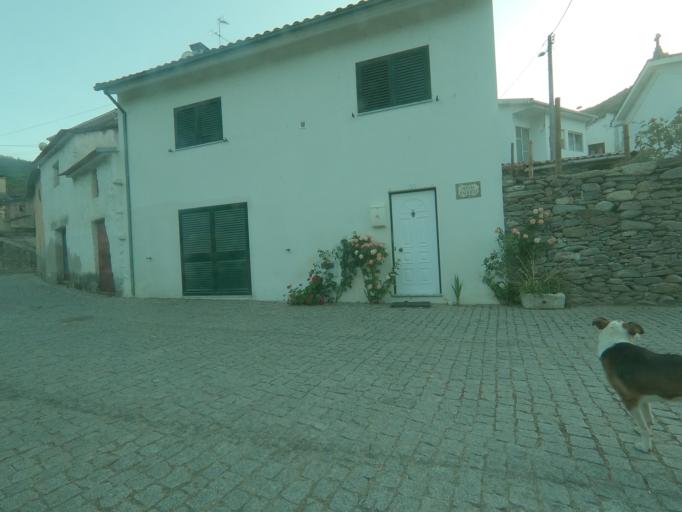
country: PT
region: Viseu
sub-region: Armamar
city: Armamar
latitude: 41.1275
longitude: -7.6977
